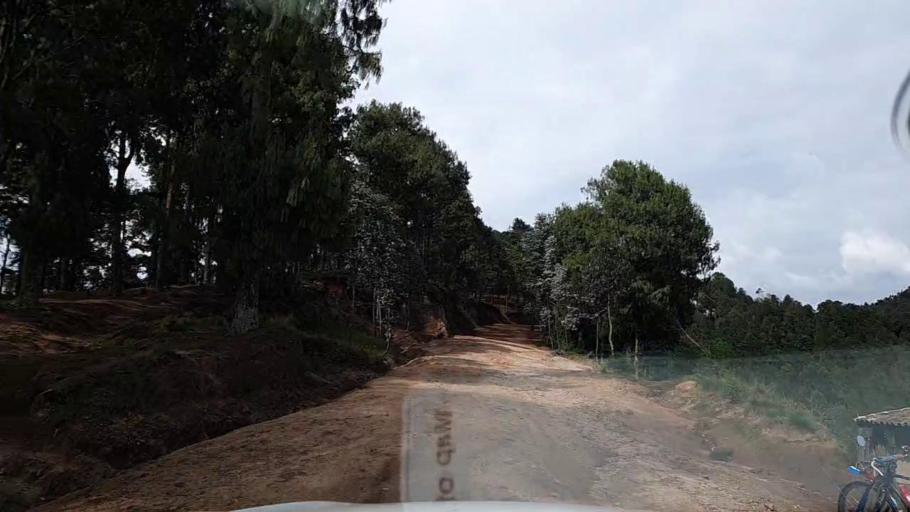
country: RW
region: Southern Province
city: Nzega
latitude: -2.4135
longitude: 29.4534
